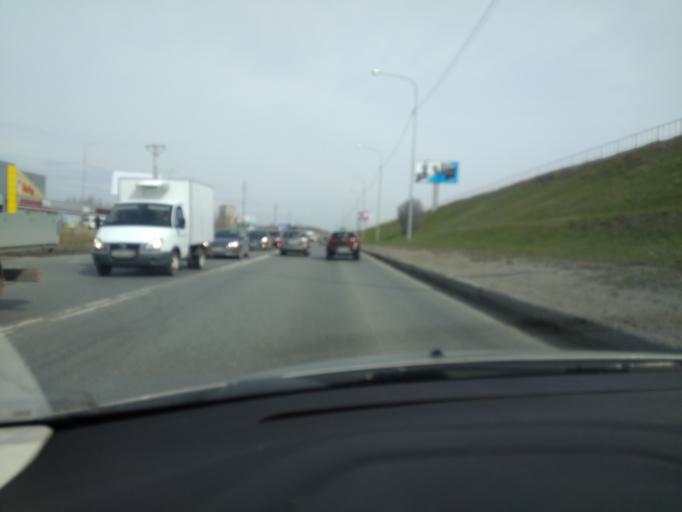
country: RU
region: Tjumen
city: Melioratorov
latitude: 57.1646
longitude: 65.6004
